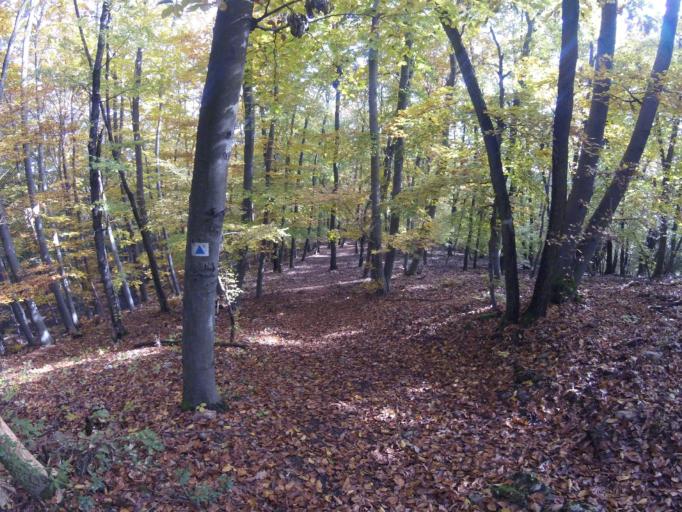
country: HU
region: Borsod-Abauj-Zemplen
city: Putnok
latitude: 48.2185
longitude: 20.4525
